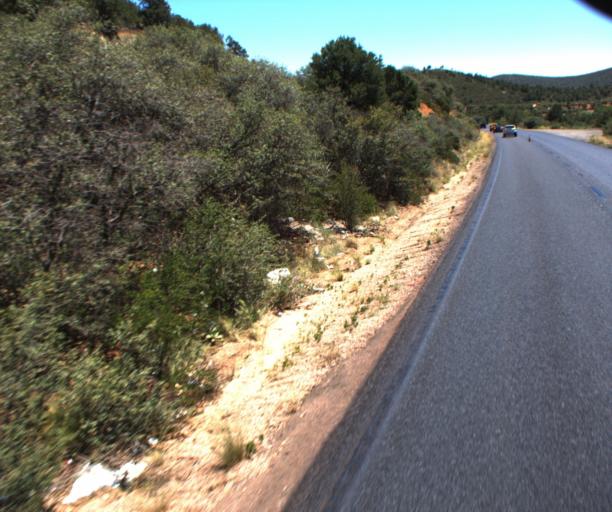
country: US
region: Arizona
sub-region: Gila County
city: Payson
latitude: 34.1997
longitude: -111.3306
